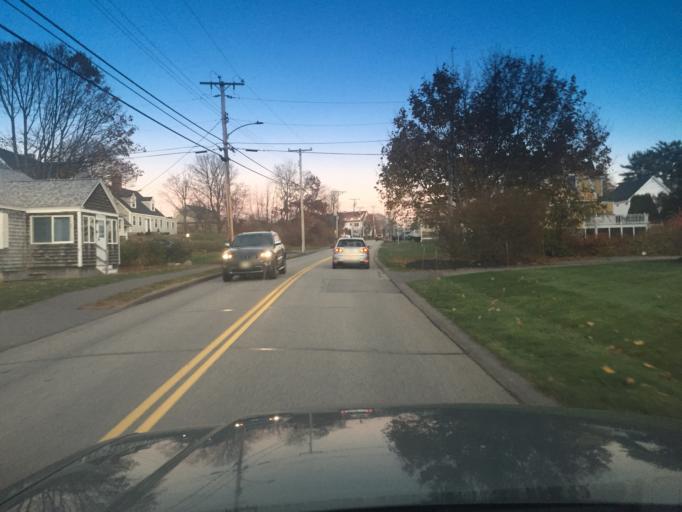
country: US
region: Maine
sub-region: York County
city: York Beach
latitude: 43.1724
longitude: -70.6021
